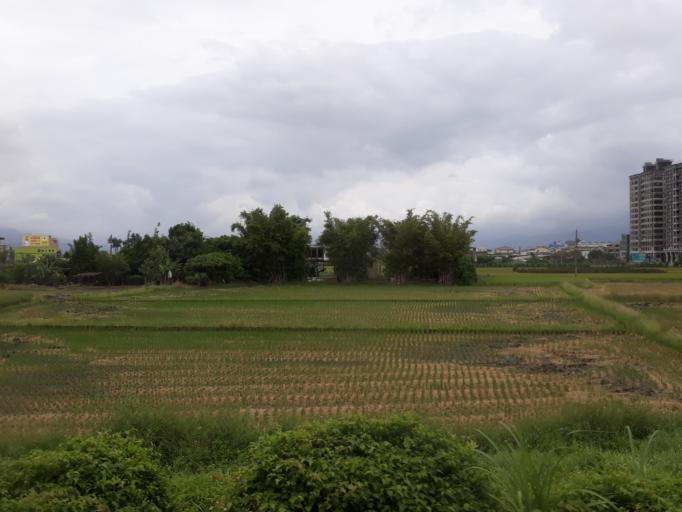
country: TW
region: Taiwan
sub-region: Yilan
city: Yilan
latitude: 24.6886
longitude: 121.7749
